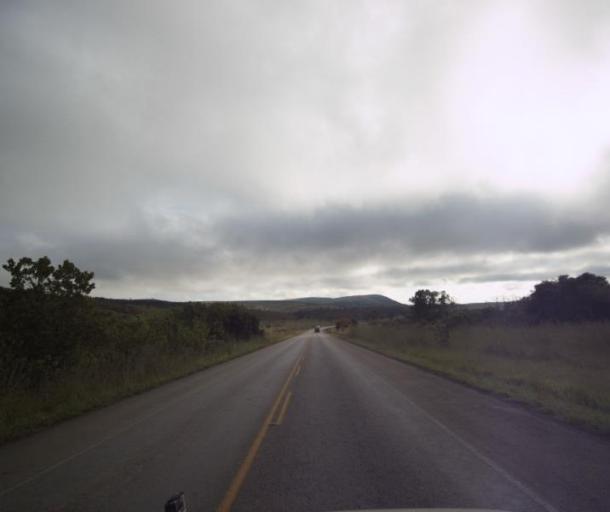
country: BR
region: Goias
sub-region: Pirenopolis
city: Pirenopolis
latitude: -15.7419
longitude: -48.7235
